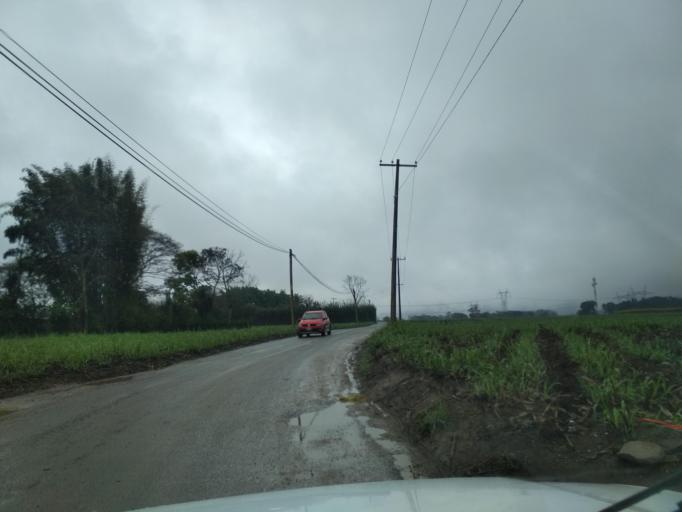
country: MX
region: Veracruz
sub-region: Amatlan de los Reyes
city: Centro de Readaptacion Social
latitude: 18.8313
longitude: -96.9307
